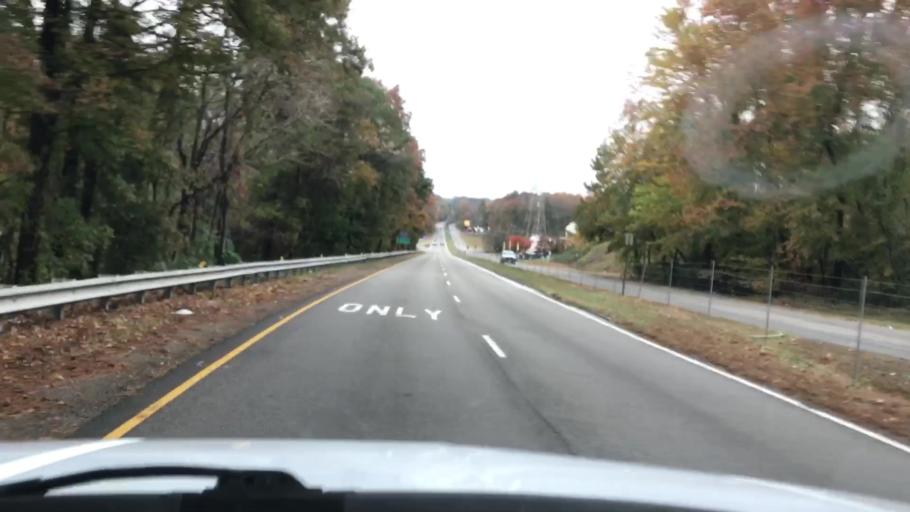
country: US
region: Virginia
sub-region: Henrico County
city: Chamberlayne
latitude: 37.6113
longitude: -77.4466
